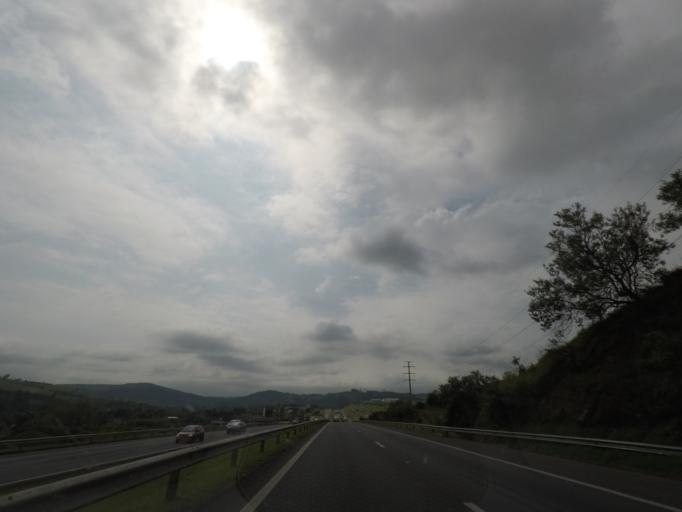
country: BR
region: Sao Paulo
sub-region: Valinhos
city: Valinhos
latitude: -22.9061
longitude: -46.9764
